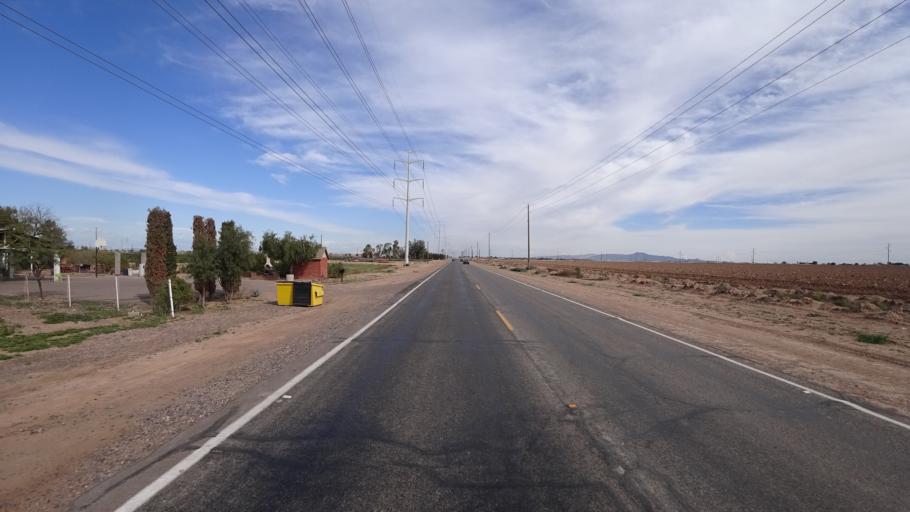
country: US
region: Arizona
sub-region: Maricopa County
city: Tolleson
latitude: 33.4064
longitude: -112.2974
